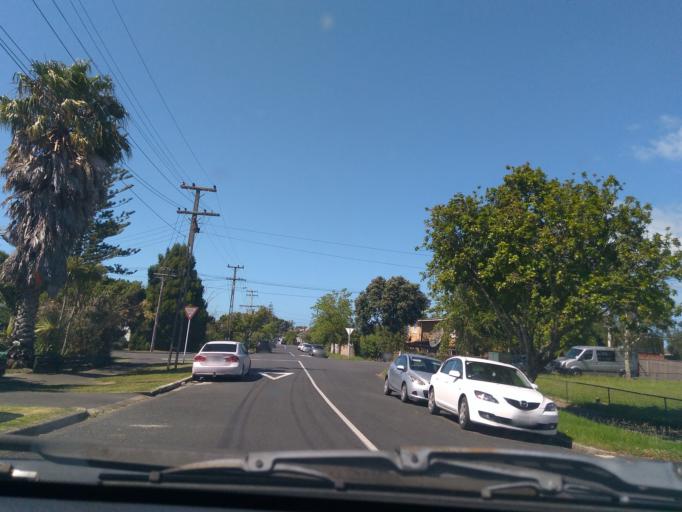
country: NZ
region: Auckland
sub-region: Auckland
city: Rosebank
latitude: -36.8797
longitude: 174.6988
